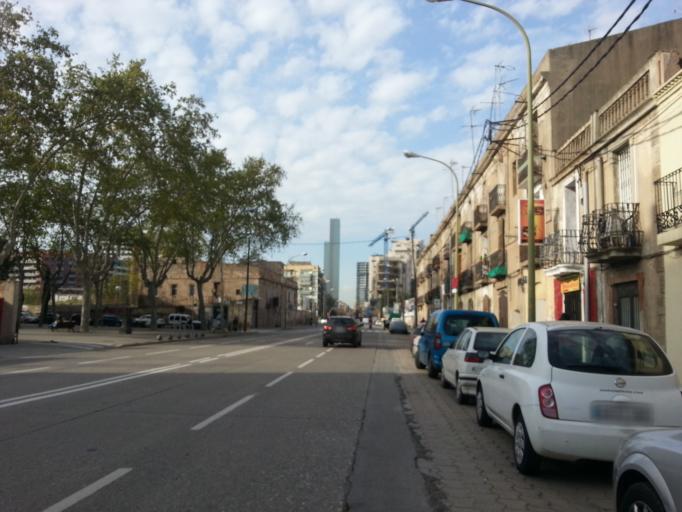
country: ES
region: Catalonia
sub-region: Provincia de Barcelona
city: Sant Marti
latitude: 41.4117
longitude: 2.2043
